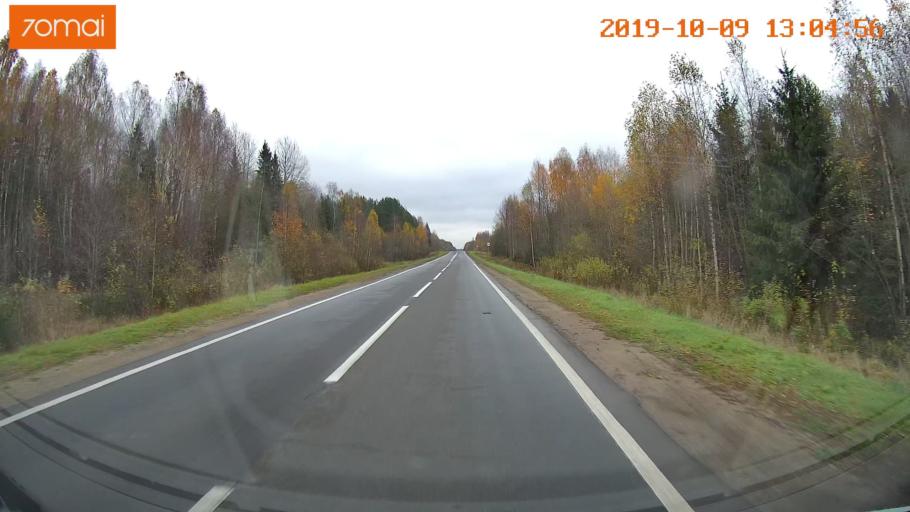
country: RU
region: Jaroslavl
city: Lyubim
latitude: 58.3579
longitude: 40.5674
